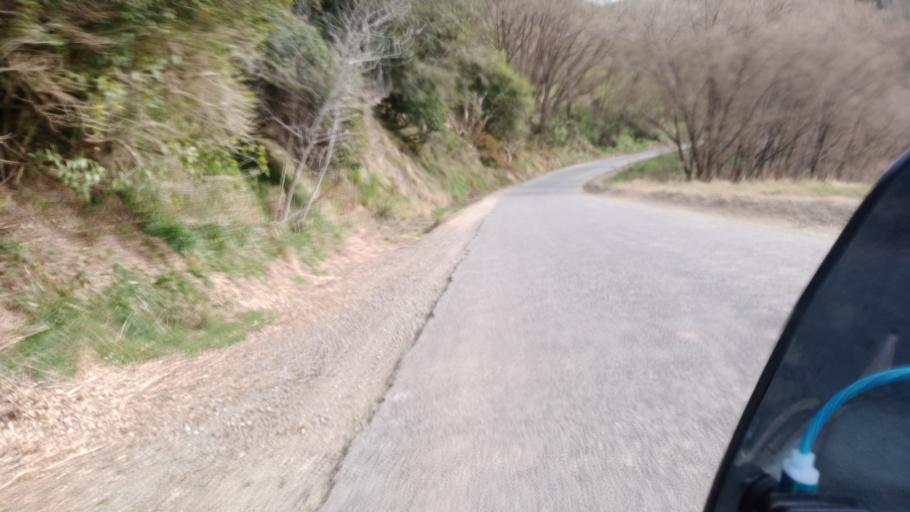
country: NZ
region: Hawke's Bay
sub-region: Wairoa District
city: Wairoa
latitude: -38.8030
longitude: 177.4480
